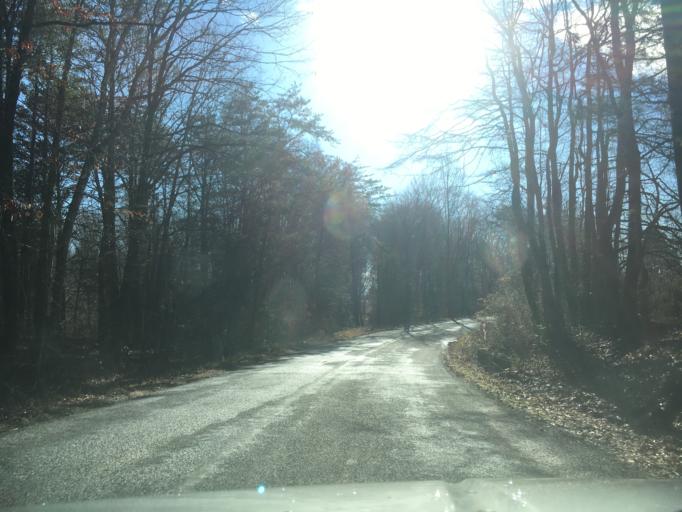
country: US
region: Virginia
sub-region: Fauquier County
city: Bealeton
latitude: 38.4446
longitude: -77.6487
